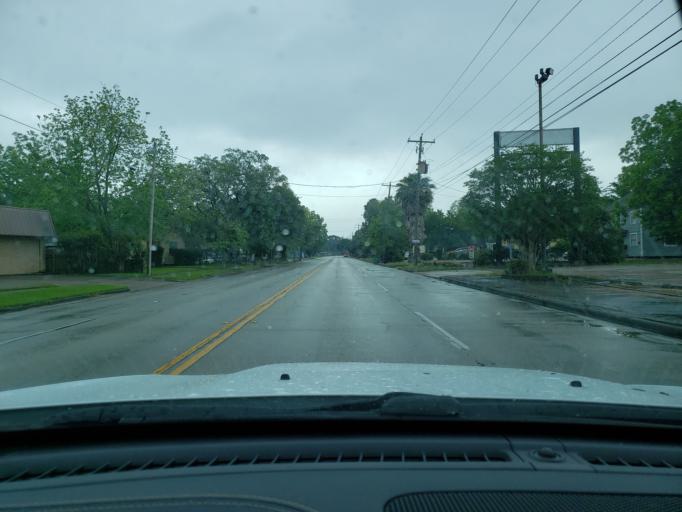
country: US
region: Texas
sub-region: Harris County
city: Baytown
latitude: 29.7431
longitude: -94.9718
